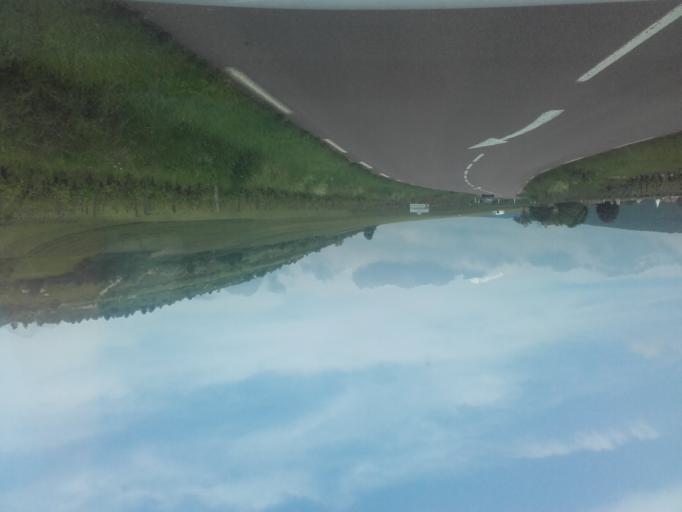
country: FR
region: Bourgogne
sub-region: Departement de la Cote-d'Or
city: Meursault
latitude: 46.9888
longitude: 4.7597
